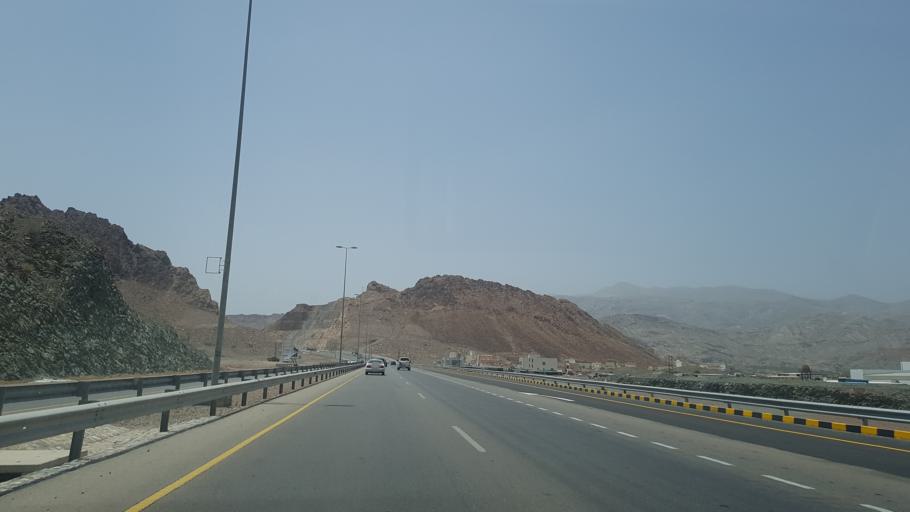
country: OM
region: Muhafazat ad Dakhiliyah
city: Bidbid
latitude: 23.4623
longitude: 58.1208
